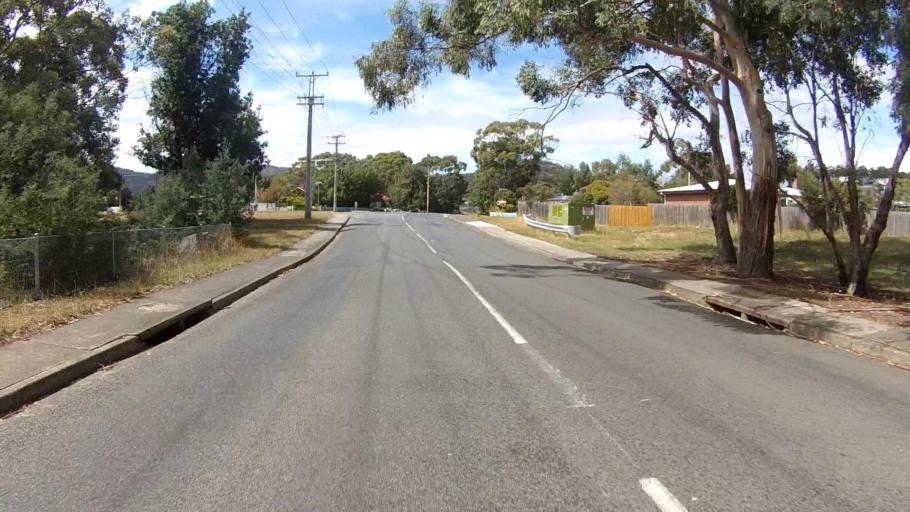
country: AU
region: Tasmania
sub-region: Clarence
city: Lindisfarne
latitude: -42.8090
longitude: 147.3502
